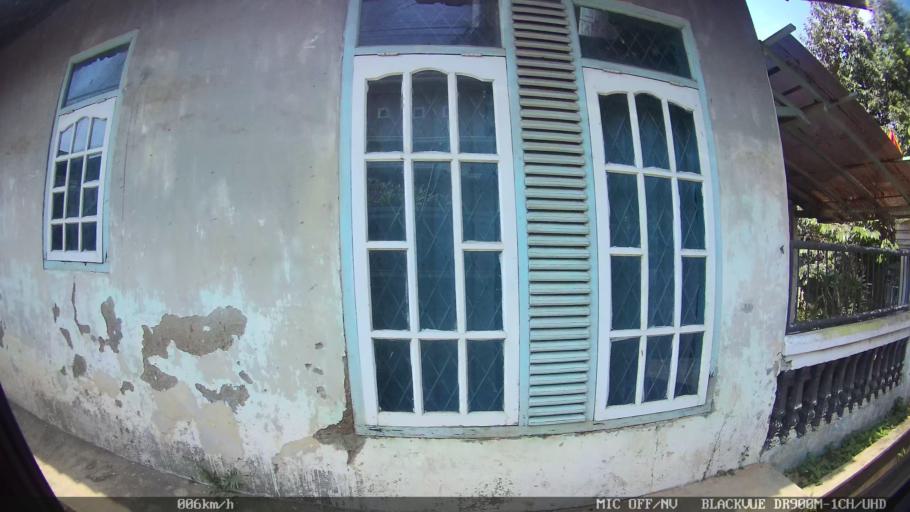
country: ID
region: Lampung
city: Kedaton
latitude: -5.3972
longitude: 105.2321
